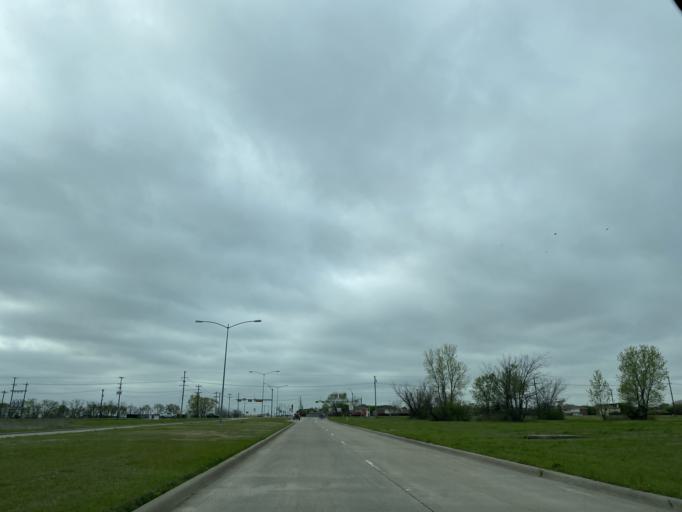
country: US
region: Texas
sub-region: Collin County
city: Parker
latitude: 33.1021
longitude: -96.6204
